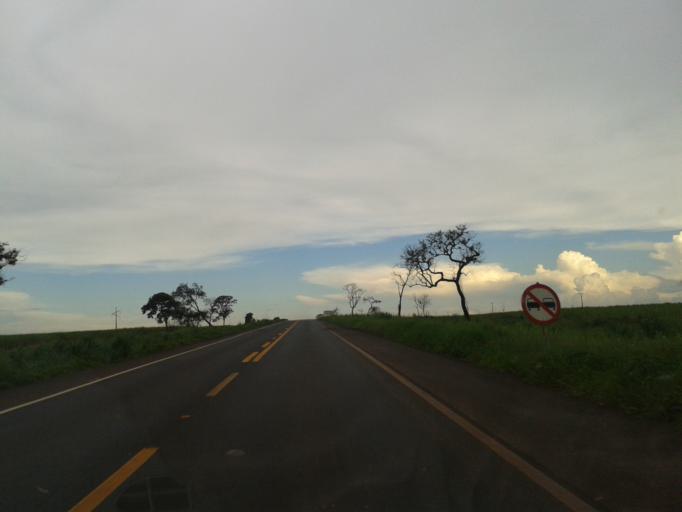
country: BR
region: Minas Gerais
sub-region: Santa Vitoria
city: Santa Vitoria
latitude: -18.8959
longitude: -50.1777
